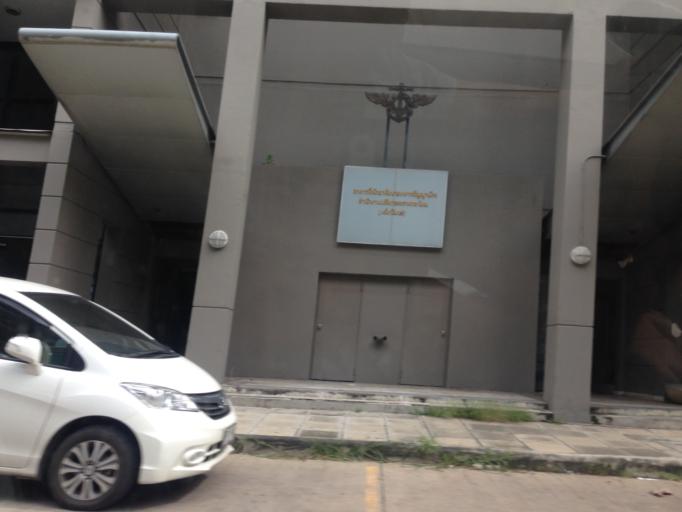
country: TH
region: Nonthaburi
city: Pak Kret
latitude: 13.9243
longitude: 100.5359
